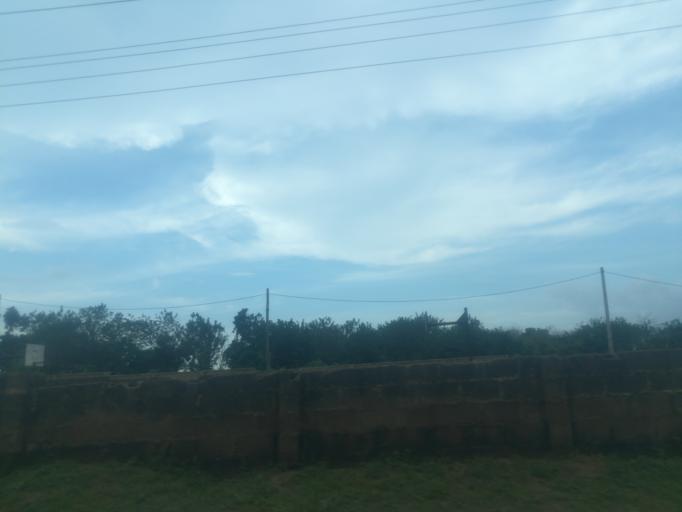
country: NG
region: Oyo
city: Ibadan
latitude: 7.4315
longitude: 3.8960
